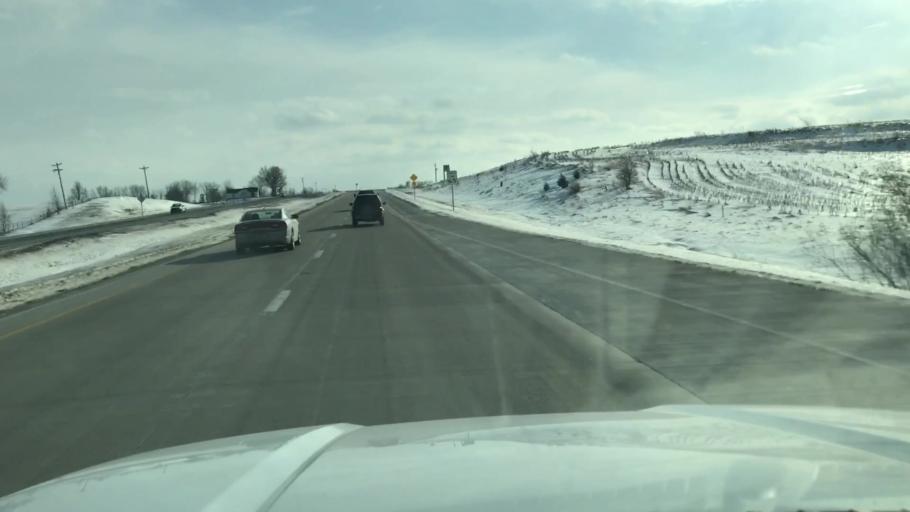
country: US
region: Missouri
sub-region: Nodaway County
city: Maryville
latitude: 40.3046
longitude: -94.8748
